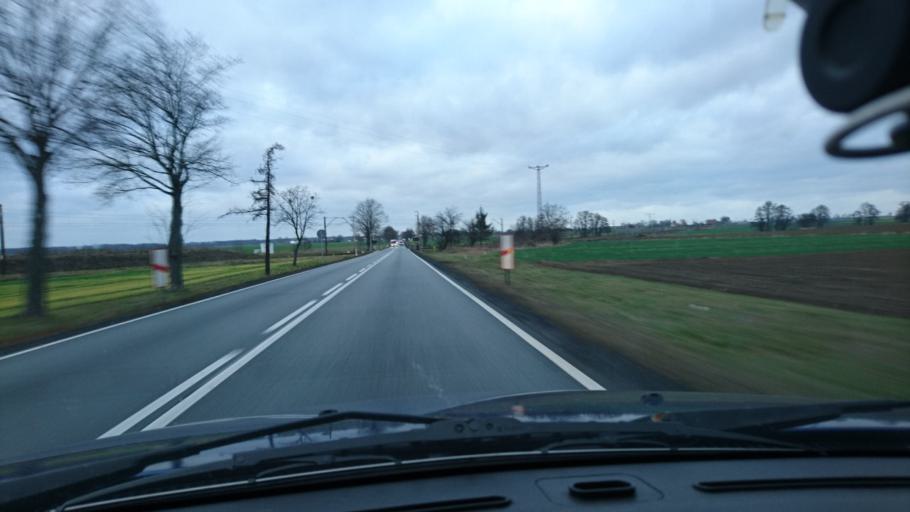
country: PL
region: Opole Voivodeship
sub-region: Powiat kluczborski
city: Kluczbork
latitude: 51.0150
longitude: 18.2007
